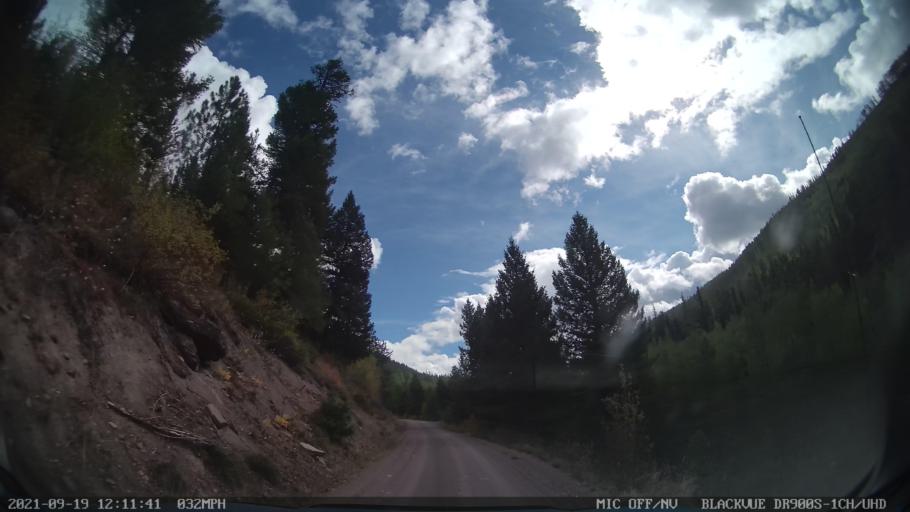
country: US
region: Montana
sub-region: Missoula County
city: Seeley Lake
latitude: 47.1733
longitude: -113.3714
